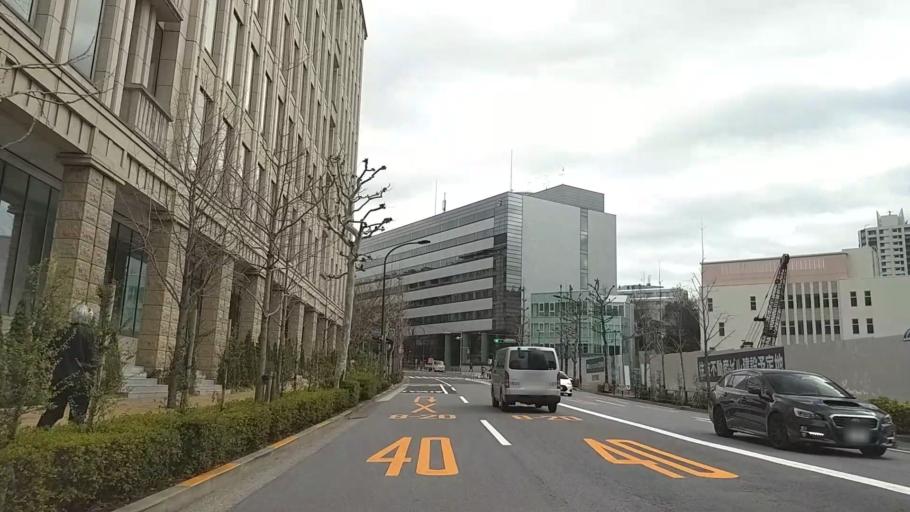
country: JP
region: Tokyo
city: Tokyo
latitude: 35.6246
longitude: 139.7319
